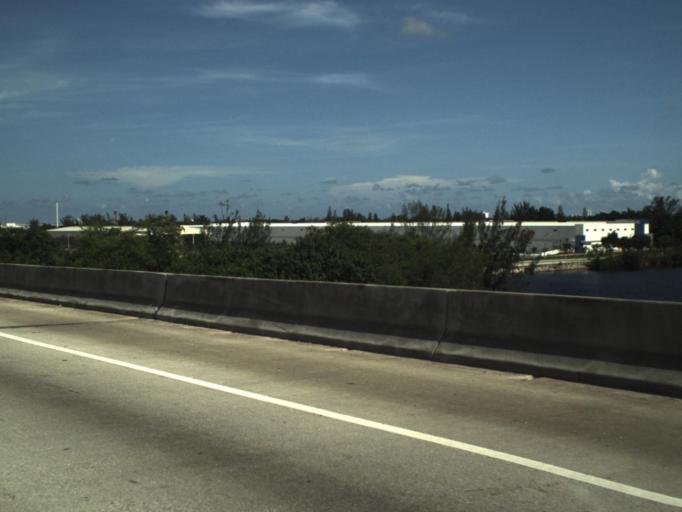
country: US
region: Florida
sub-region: Broward County
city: Broadview Park
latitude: 26.0837
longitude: -80.1830
